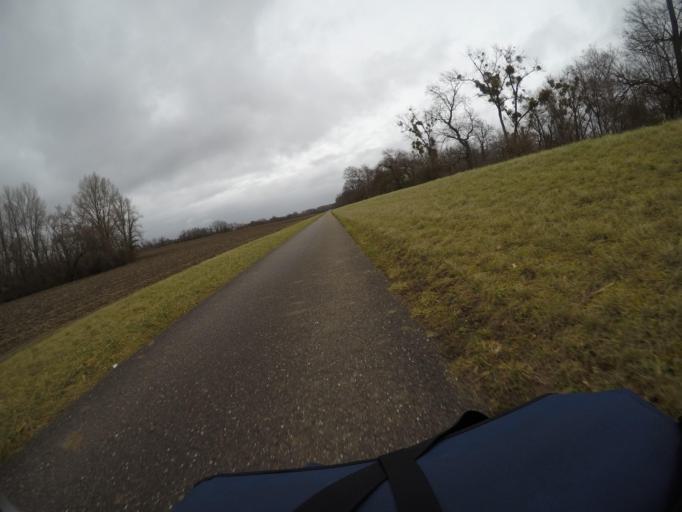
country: DE
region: Rheinland-Pfalz
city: Leimersheim
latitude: 49.1094
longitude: 8.3521
